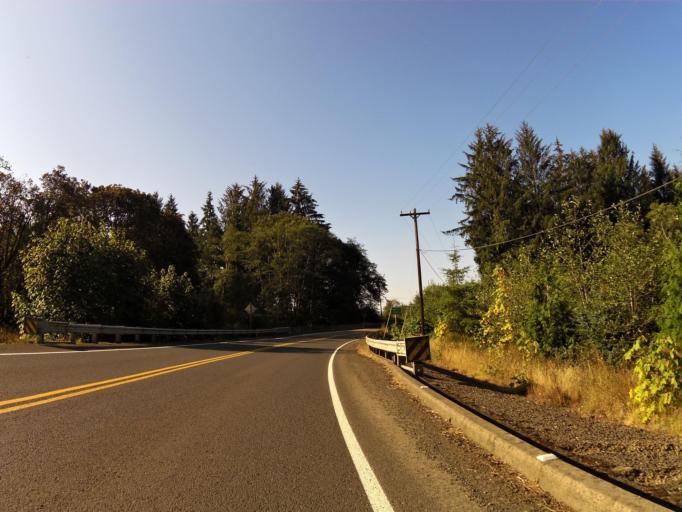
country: US
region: Oregon
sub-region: Tillamook County
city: Tillamook
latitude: 45.3864
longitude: -123.7950
